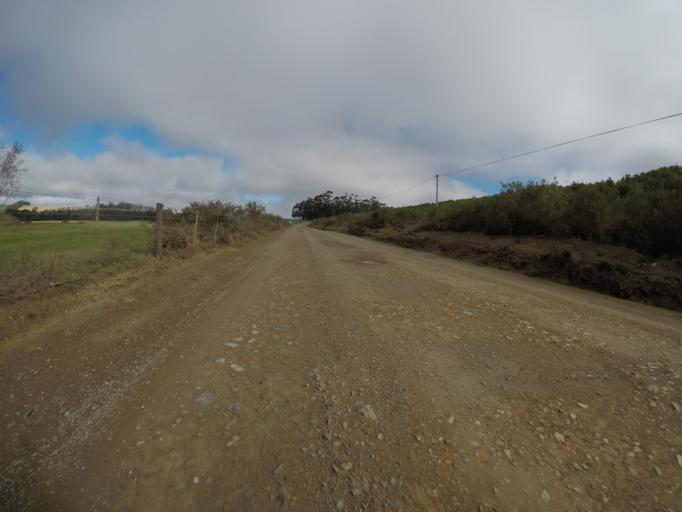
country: ZA
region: Western Cape
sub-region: Cape Winelands District Municipality
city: Ashton
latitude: -34.1253
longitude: 19.8251
